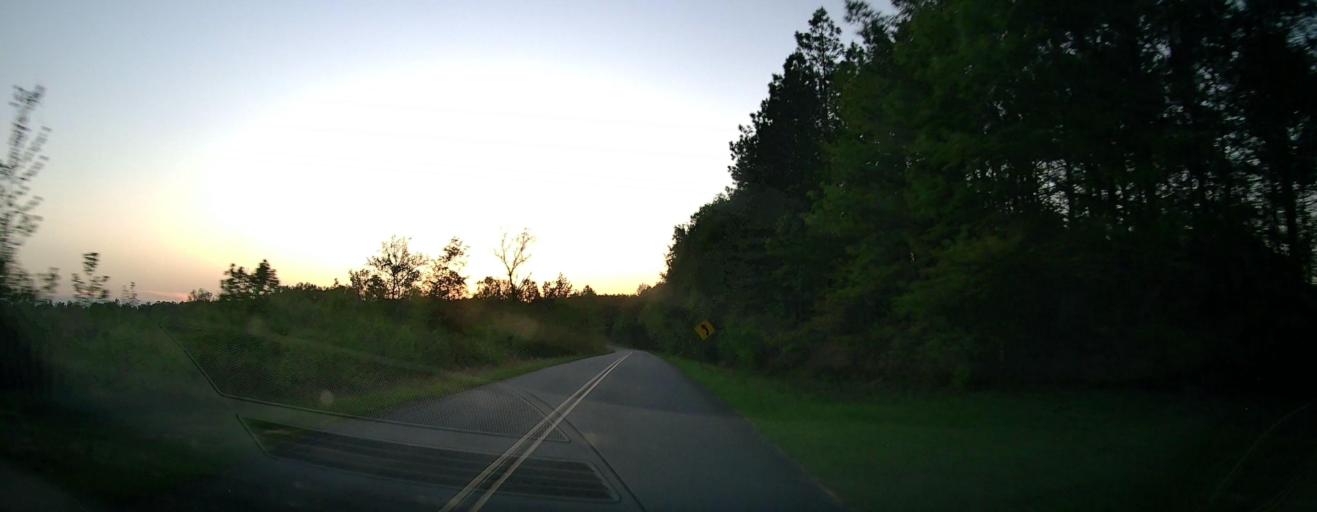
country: US
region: Georgia
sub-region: Marion County
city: Buena Vista
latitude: 32.2560
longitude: -84.5891
